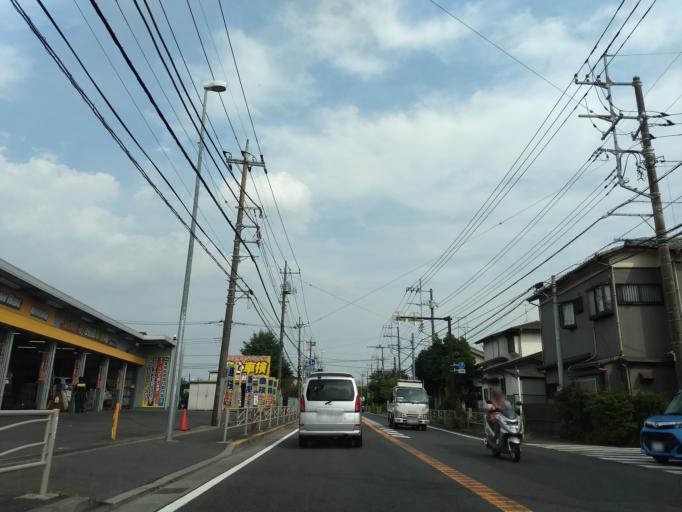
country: JP
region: Kanagawa
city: Minami-rinkan
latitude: 35.4924
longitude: 139.5119
